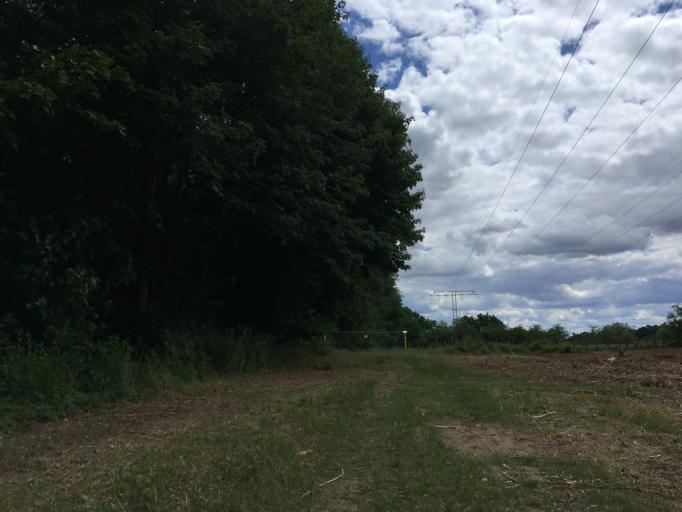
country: DE
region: Brandenburg
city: Bernau bei Berlin
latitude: 52.6935
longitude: 13.5440
